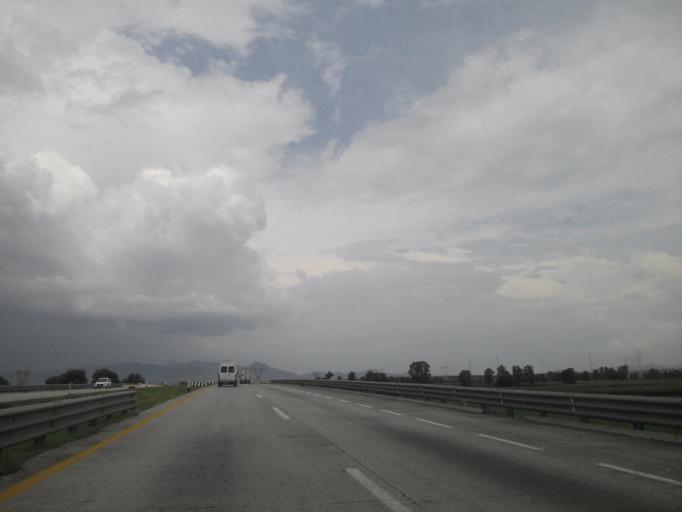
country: MX
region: Hidalgo
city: Doxey
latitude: 20.0973
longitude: -99.2769
